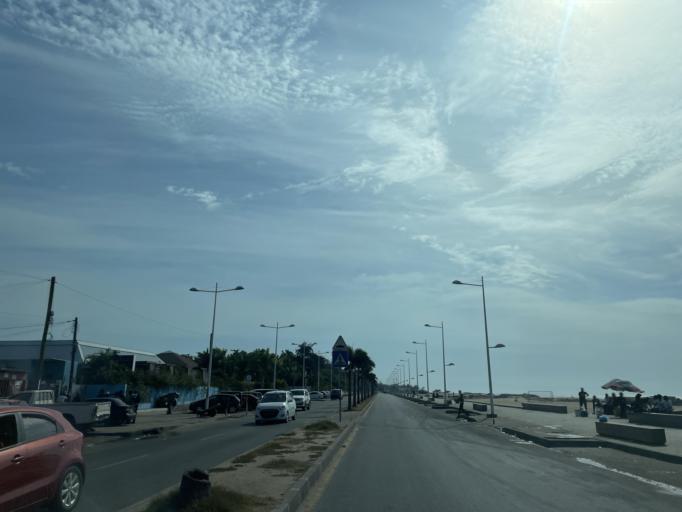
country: AO
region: Luanda
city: Luanda
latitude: -8.7728
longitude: 13.2492
